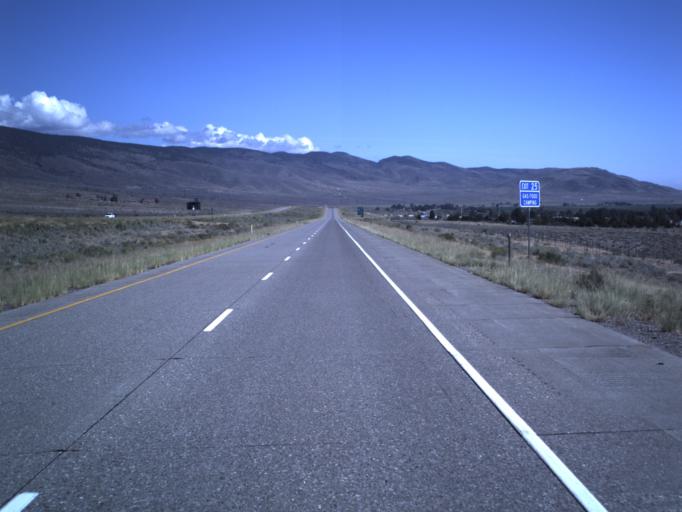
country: US
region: Utah
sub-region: Sevier County
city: Monroe
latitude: 38.6141
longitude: -112.2303
